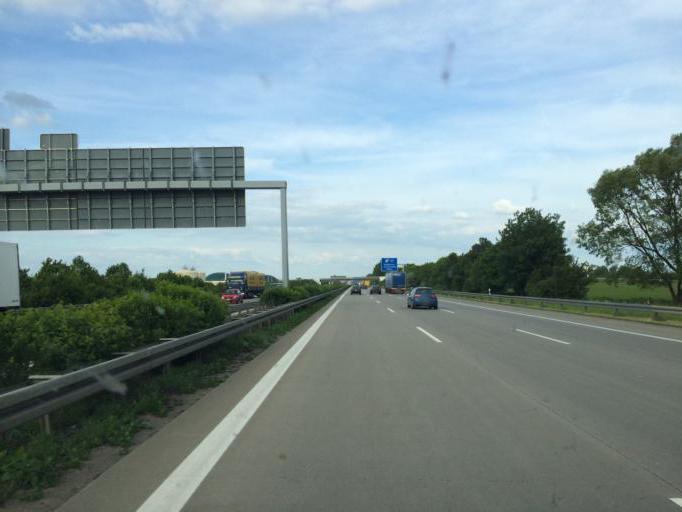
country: DE
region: Saxony-Anhalt
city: Ebendorf
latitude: 52.1718
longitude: 11.5629
